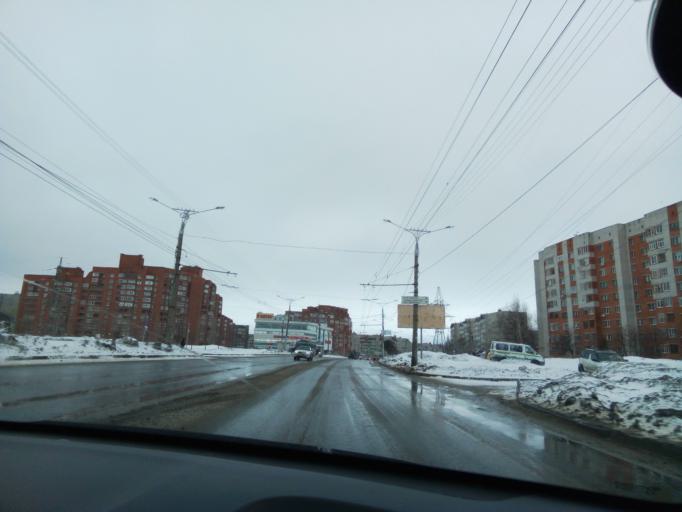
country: RU
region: Chuvashia
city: Novyye Lapsary
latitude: 56.1348
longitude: 47.1643
